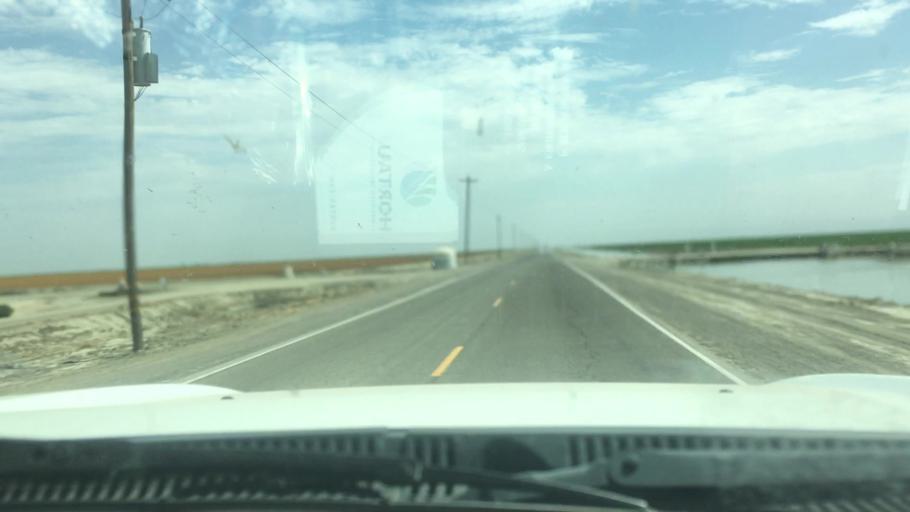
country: US
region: California
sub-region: Tulare County
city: Alpaugh
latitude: 35.9066
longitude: -119.5733
